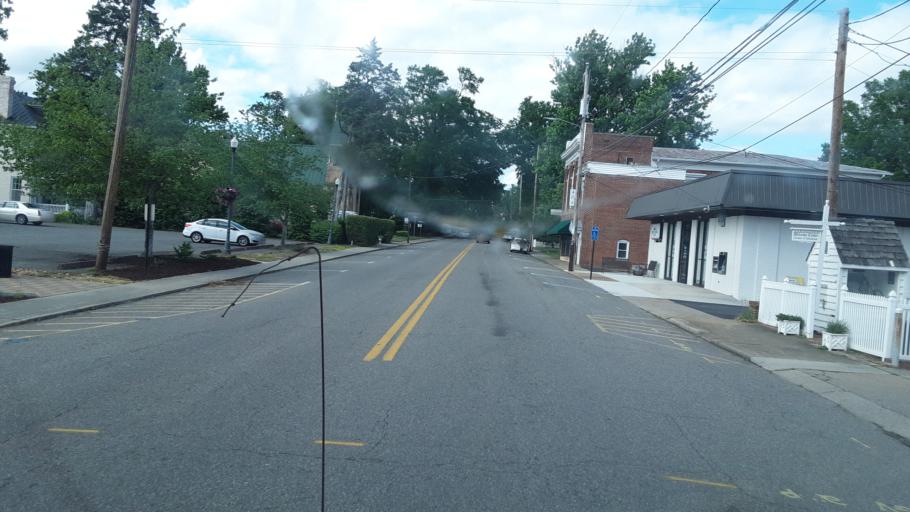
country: US
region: Virginia
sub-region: Pittsylvania County
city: Chatham
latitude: 36.8273
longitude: -79.3982
